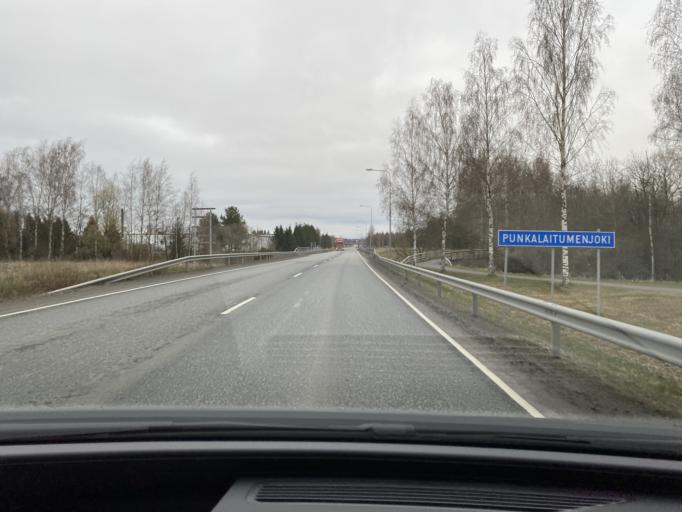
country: FI
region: Satakunta
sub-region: Pori
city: Huittinen
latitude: 61.1860
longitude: 22.6861
